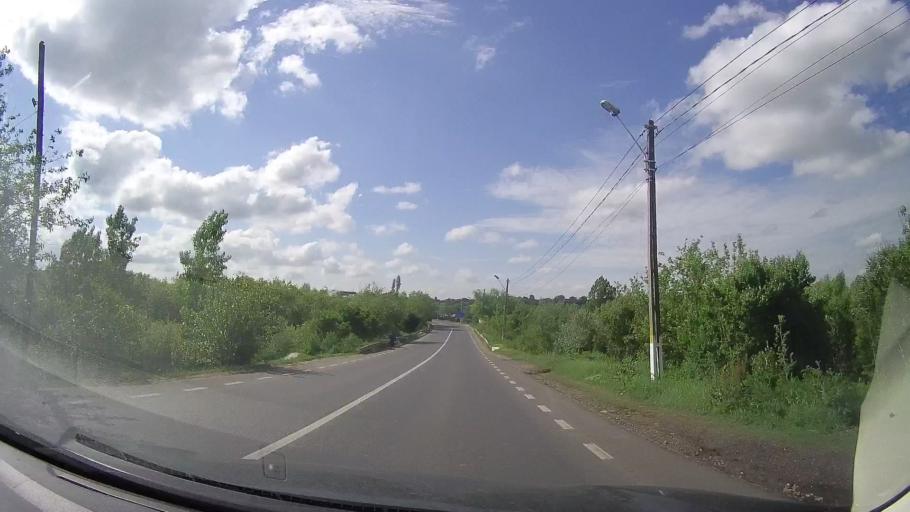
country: RO
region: Giurgiu
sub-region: Comuna Ghimpati
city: Naipu
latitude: 44.1567
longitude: 25.7593
